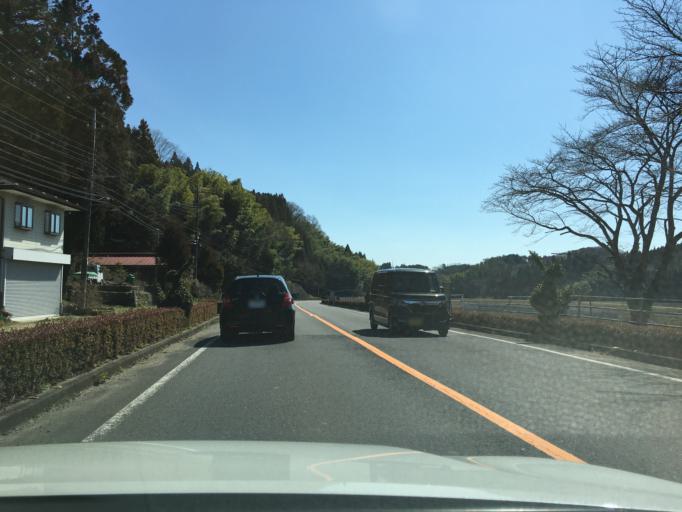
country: JP
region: Tochigi
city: Kuroiso
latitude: 37.0354
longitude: 140.1727
